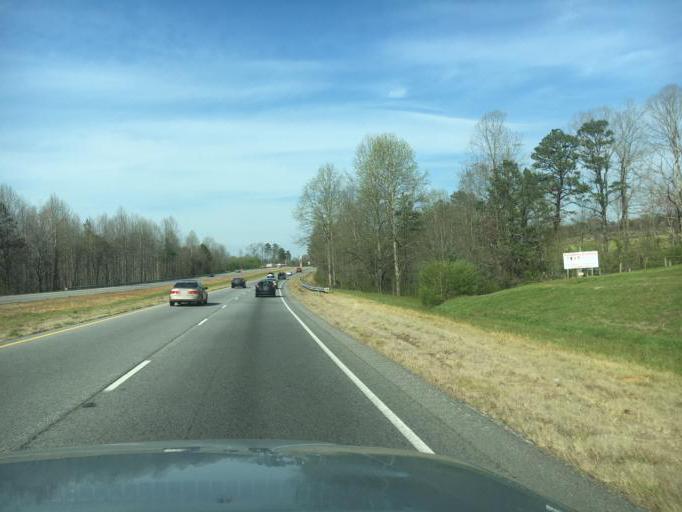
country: US
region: Georgia
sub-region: Hall County
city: Lula
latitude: 34.4233
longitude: -83.6503
